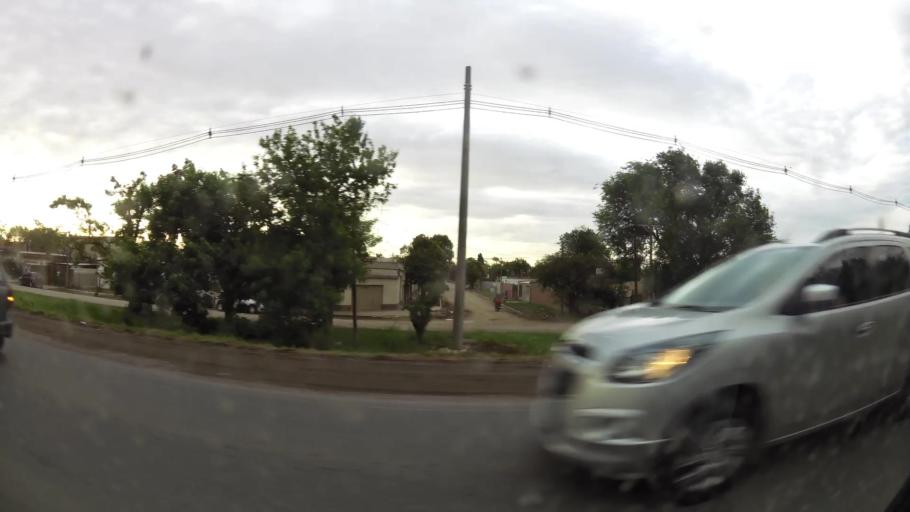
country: AR
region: Buenos Aires
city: San Nicolas de los Arroyos
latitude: -33.3674
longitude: -60.1973
